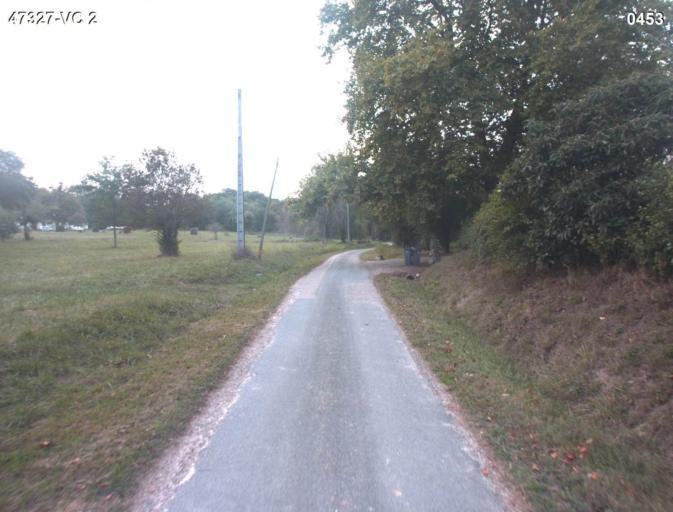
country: FR
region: Aquitaine
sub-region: Departement du Lot-et-Garonne
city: Barbaste
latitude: 44.1931
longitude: 0.2503
